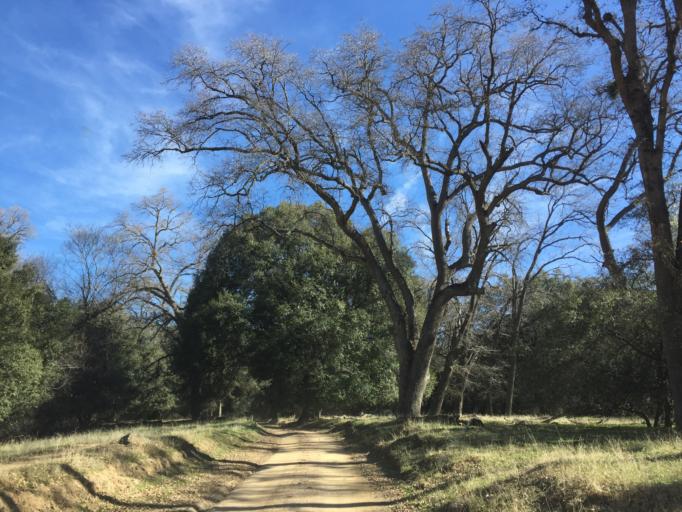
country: US
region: California
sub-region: Kern County
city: Lebec
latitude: 34.8940
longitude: -118.7414
